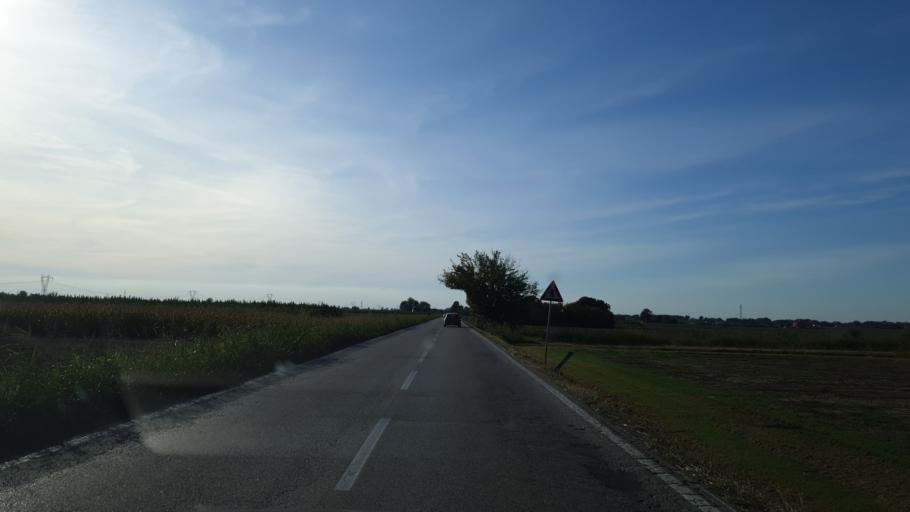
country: IT
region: Emilia-Romagna
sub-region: Provincia di Ravenna
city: Voltana
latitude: 44.5457
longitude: 11.9733
